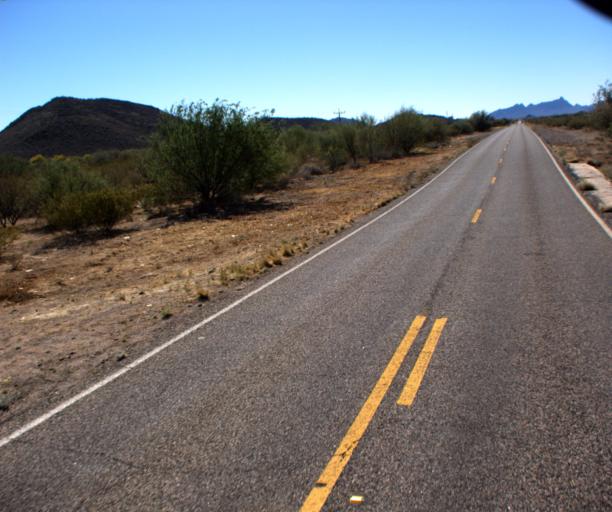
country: US
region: Arizona
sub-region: Pima County
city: Ajo
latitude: 32.2847
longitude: -112.7462
